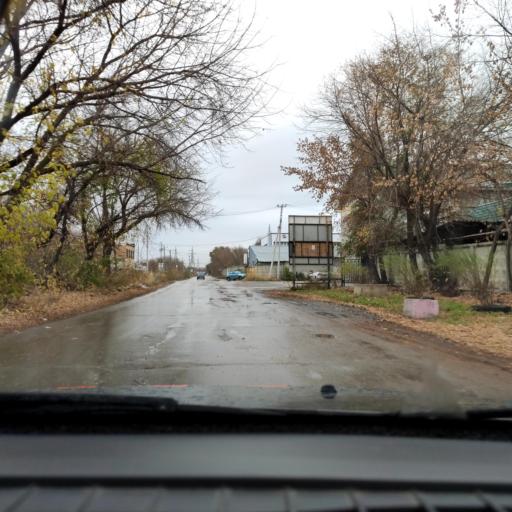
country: RU
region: Samara
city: Tol'yatti
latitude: 53.5705
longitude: 49.2844
